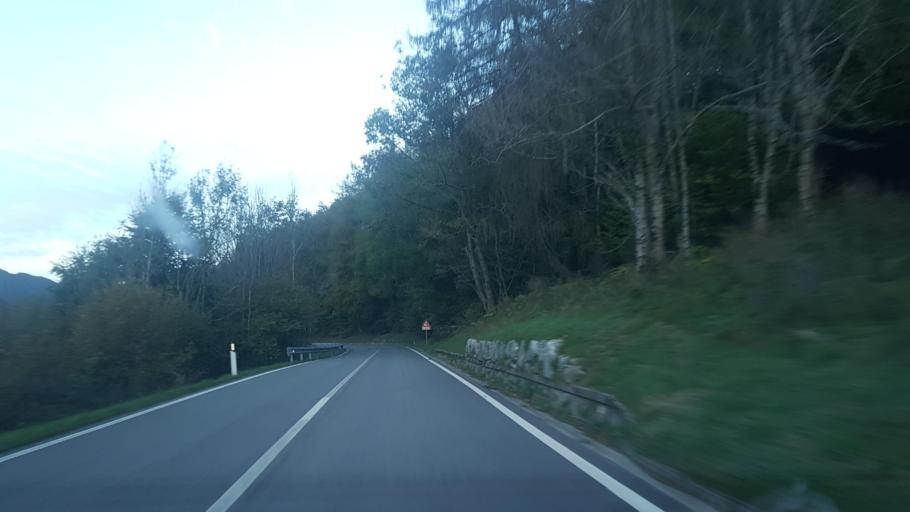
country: IT
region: Friuli Venezia Giulia
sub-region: Provincia di Udine
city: Villa Santina
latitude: 46.3586
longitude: 12.9376
